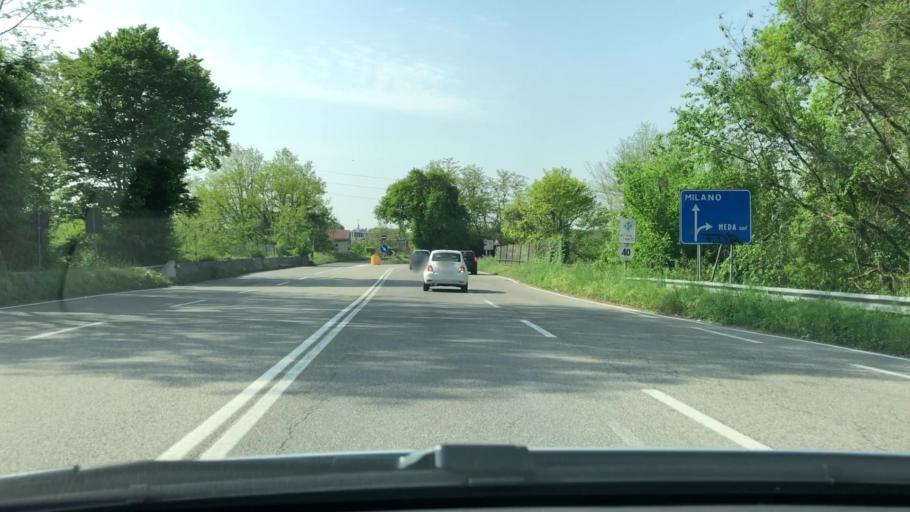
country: IT
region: Lombardy
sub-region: Provincia di Monza e Brianza
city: Meda
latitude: 45.6546
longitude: 9.1548
